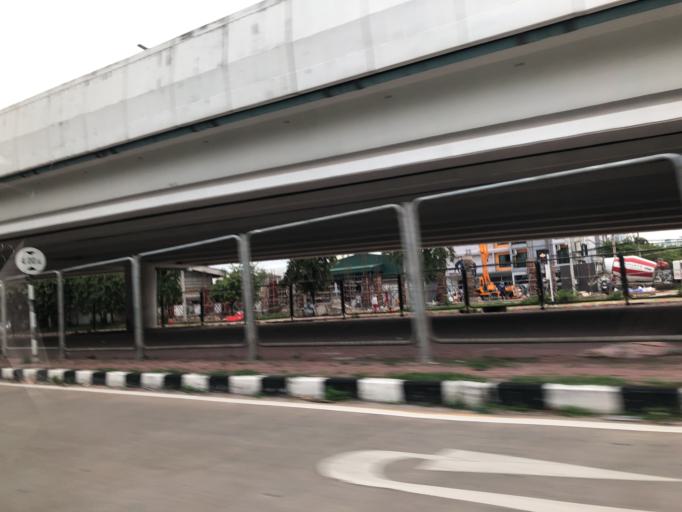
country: TH
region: Nonthaburi
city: Pak Kret
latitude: 13.9076
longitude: 100.5171
